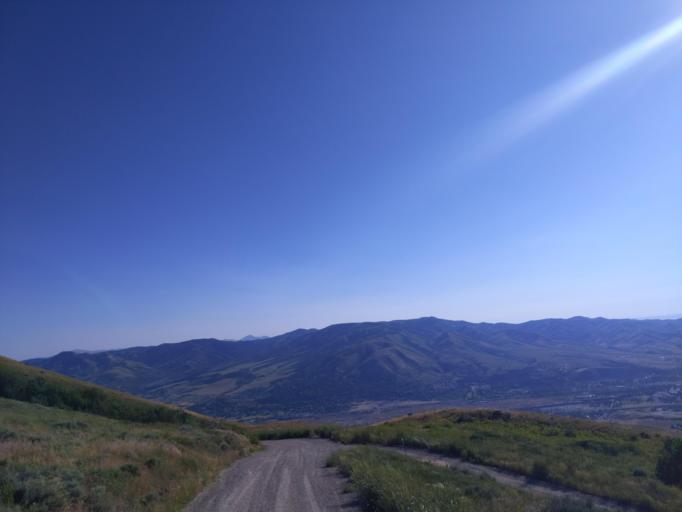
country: US
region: Idaho
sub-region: Bannock County
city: Pocatello
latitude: 42.8518
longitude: -112.3629
